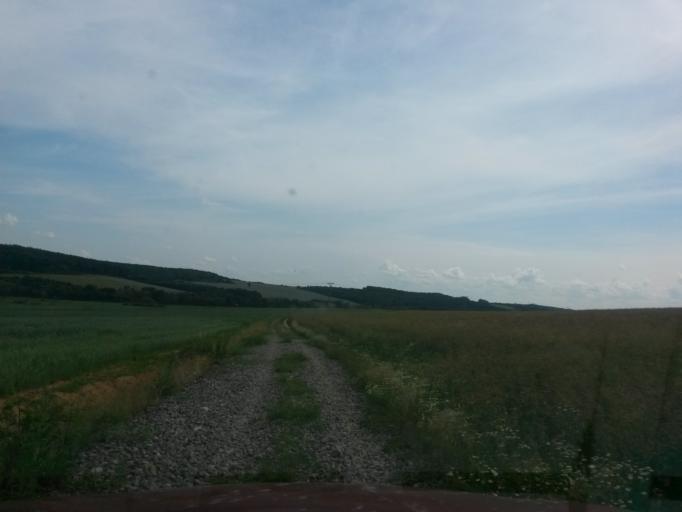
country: SK
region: Kosicky
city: Moldava nad Bodvou
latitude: 48.6612
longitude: 21.1117
